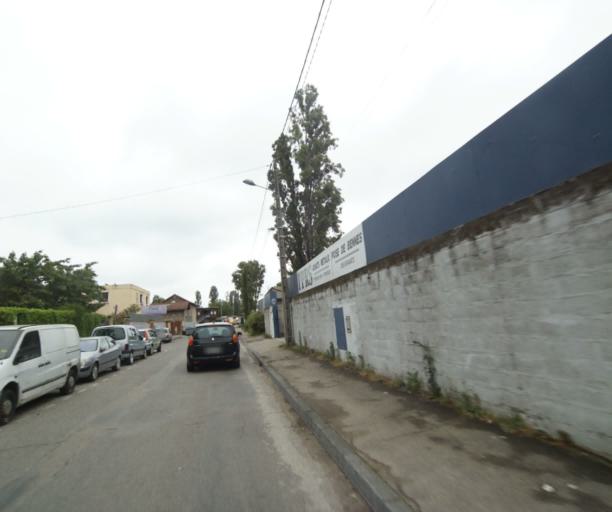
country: FR
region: Rhone-Alpes
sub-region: Departement du Rhone
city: Vaulx-en-Velin
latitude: 45.7858
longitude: 4.9005
